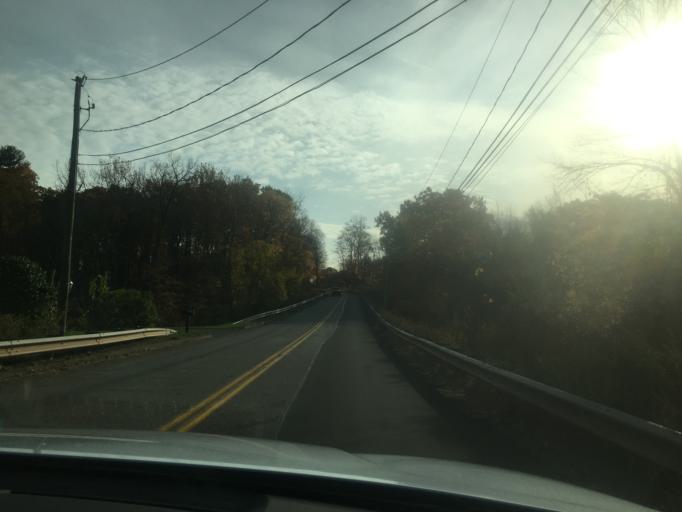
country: US
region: Connecticut
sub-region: Hartford County
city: Broad Brook
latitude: 41.8796
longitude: -72.5745
